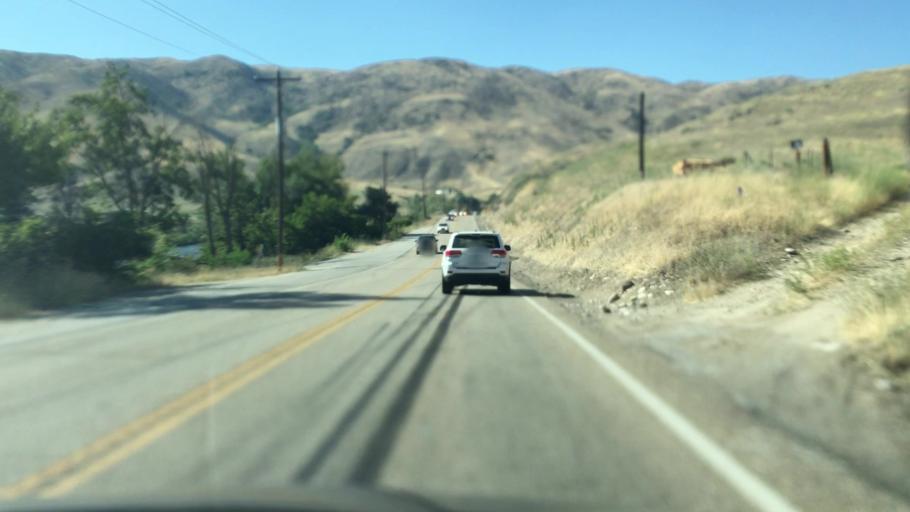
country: US
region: Idaho
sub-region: Ada County
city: Eagle
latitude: 43.9749
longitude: -116.1907
